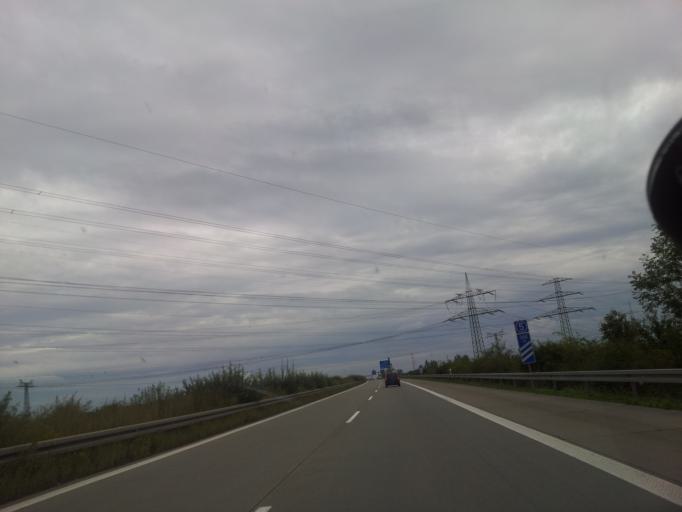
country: DE
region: Saxony-Anhalt
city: Hohendodeleben
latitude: 52.0772
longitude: 11.5468
